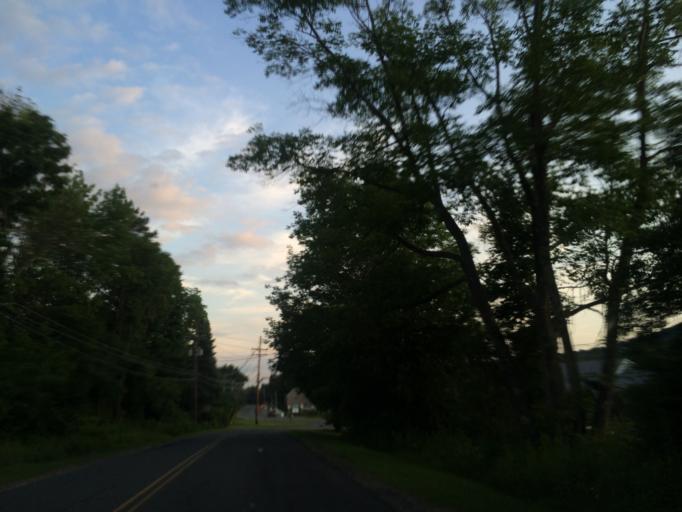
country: US
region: Massachusetts
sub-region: Berkshire County
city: Lanesborough
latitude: 42.5381
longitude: -73.2289
